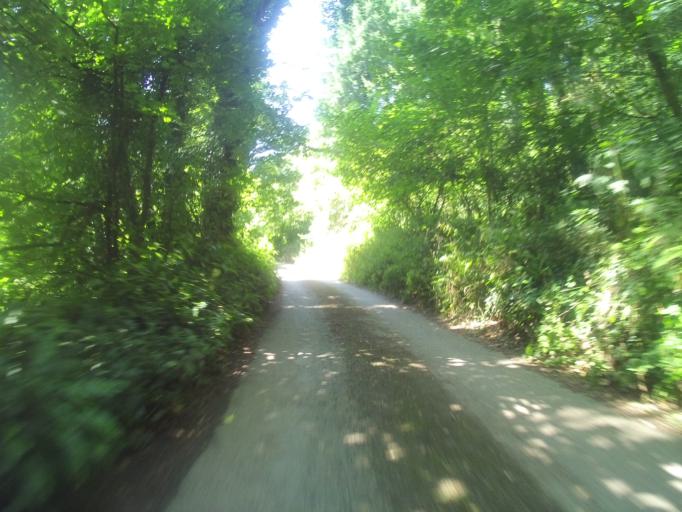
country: GB
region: England
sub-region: Devon
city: Dartmouth
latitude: 50.3580
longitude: -3.6118
